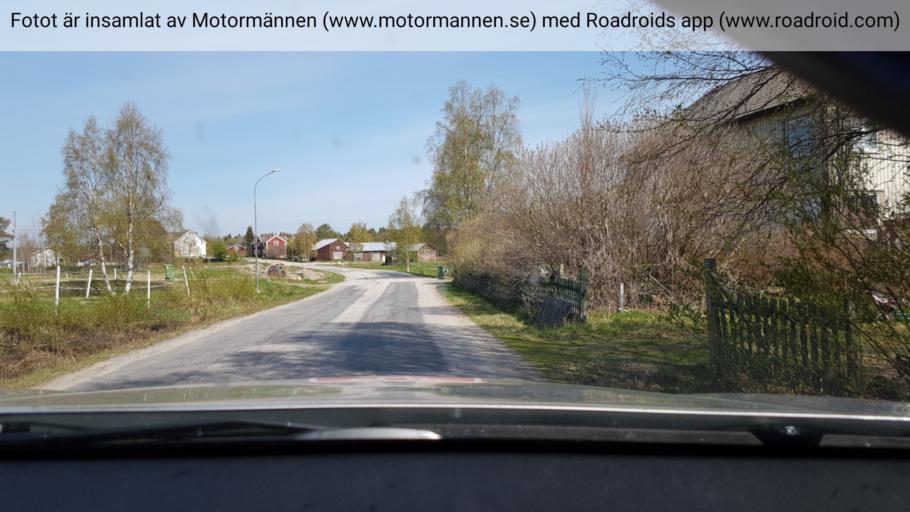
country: SE
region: Vaesterbotten
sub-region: Umea Kommun
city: Saevar
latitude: 63.8365
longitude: 20.6019
